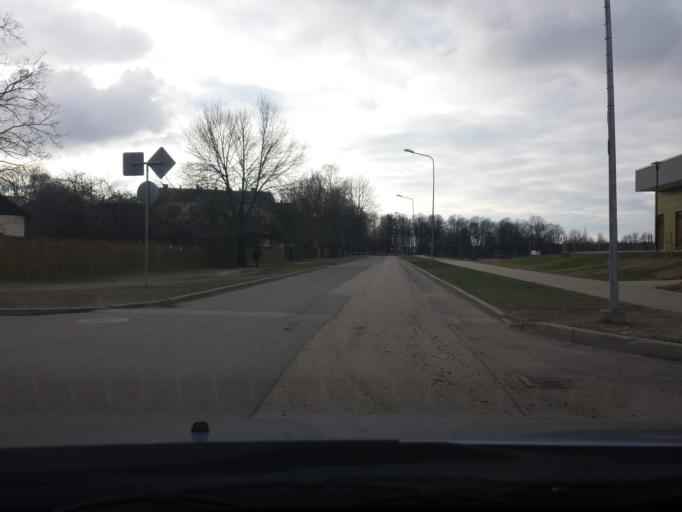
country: LV
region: Riga
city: Jaunciems
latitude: 56.9882
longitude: 24.1699
